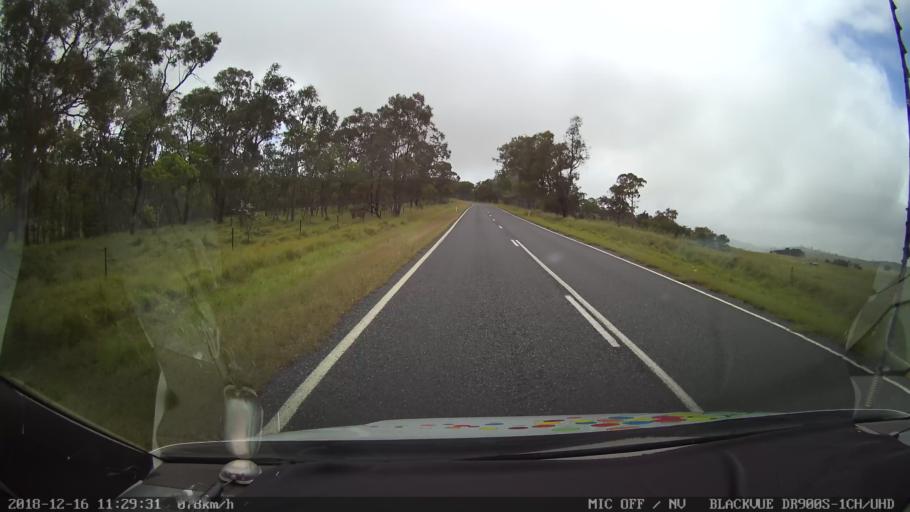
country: AU
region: New South Wales
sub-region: Tenterfield Municipality
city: Carrolls Creek
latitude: -29.0361
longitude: 152.1102
